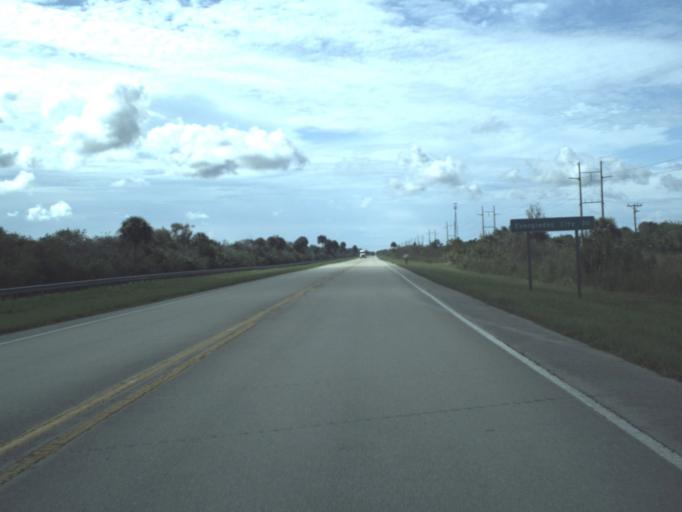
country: US
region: Florida
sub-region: Collier County
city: Immokalee
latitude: 26.1450
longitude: -81.3450
